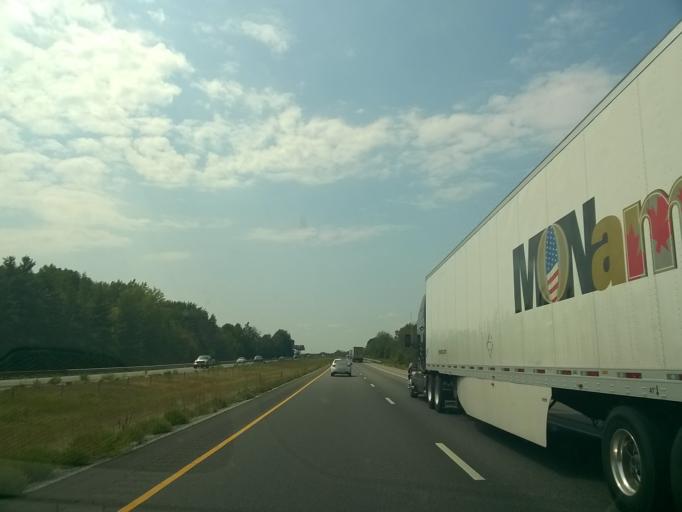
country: US
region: Indiana
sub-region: Clay County
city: Brazil
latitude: 39.4644
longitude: -87.0661
